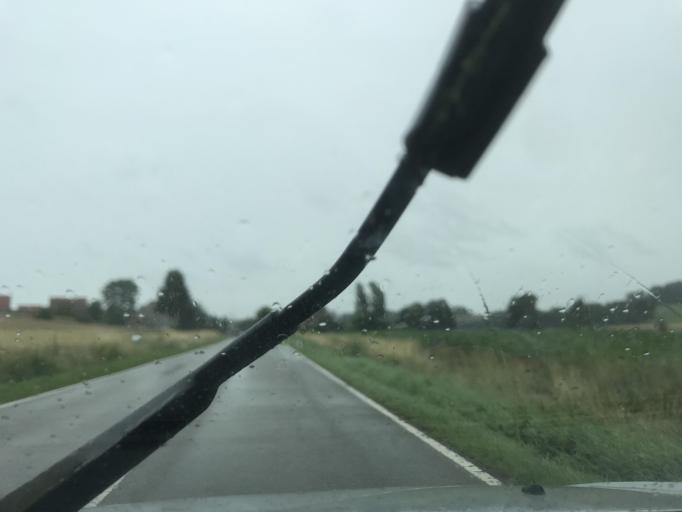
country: DE
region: Bavaria
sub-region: Upper Bavaria
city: Jetzendorf
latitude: 48.4347
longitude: 11.4500
